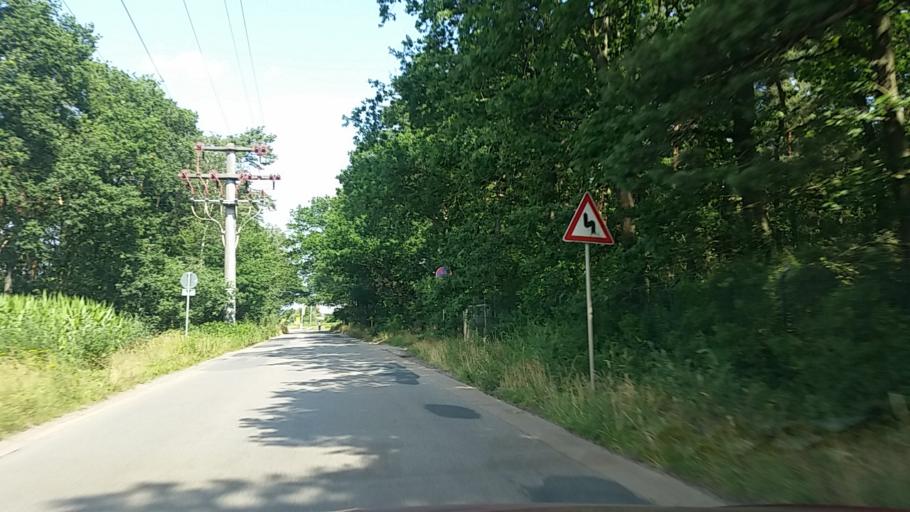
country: DE
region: Lower Saxony
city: Elze
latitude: 52.5566
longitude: 9.7745
